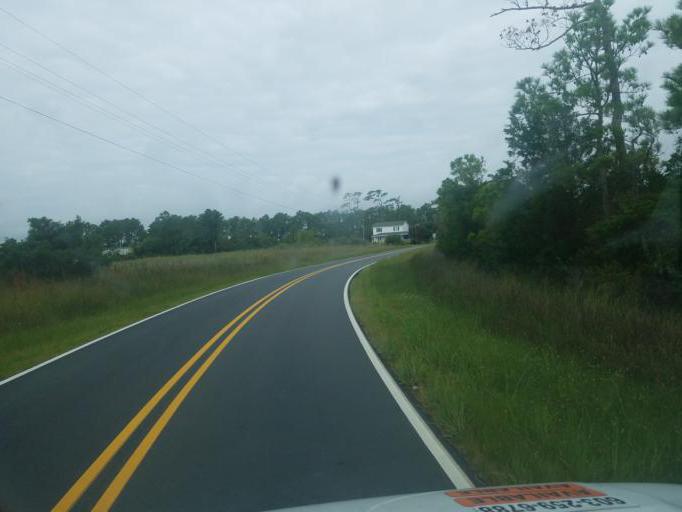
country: US
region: North Carolina
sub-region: Dare County
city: Manteo
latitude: 35.8762
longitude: -75.7569
